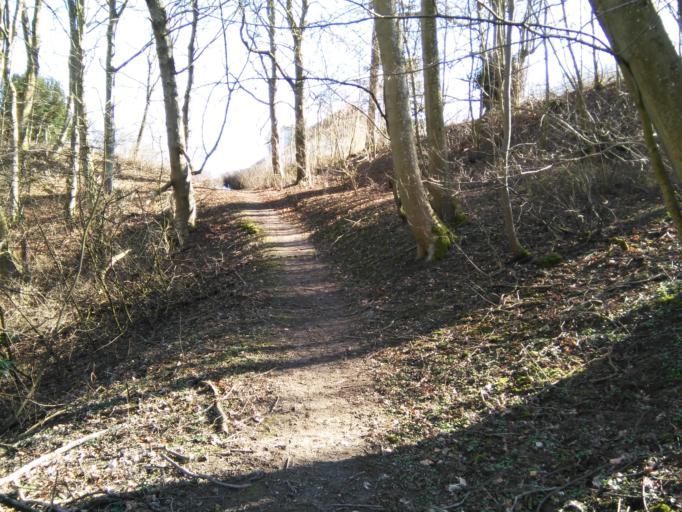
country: DK
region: Central Jutland
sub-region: Arhus Kommune
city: Beder
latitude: 56.0687
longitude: 10.1875
